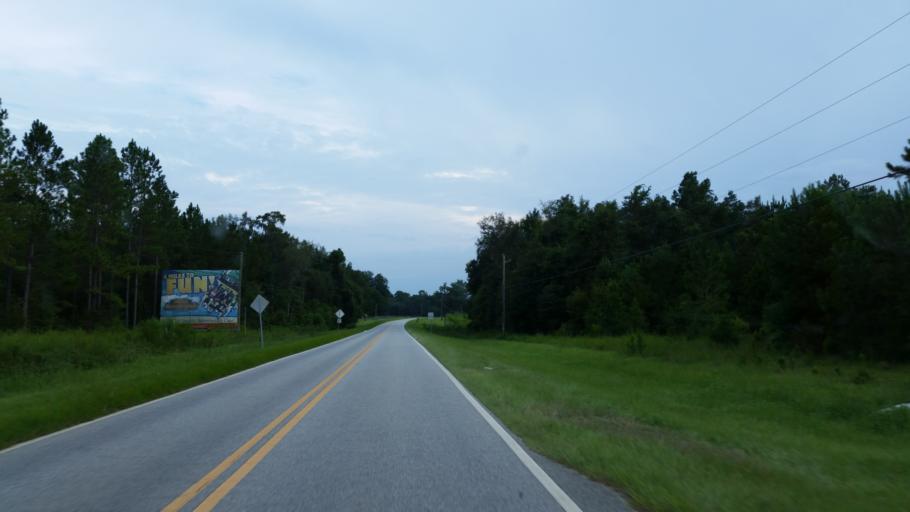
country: US
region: Georgia
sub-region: Lowndes County
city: Valdosta
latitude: 30.7704
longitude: -83.3036
